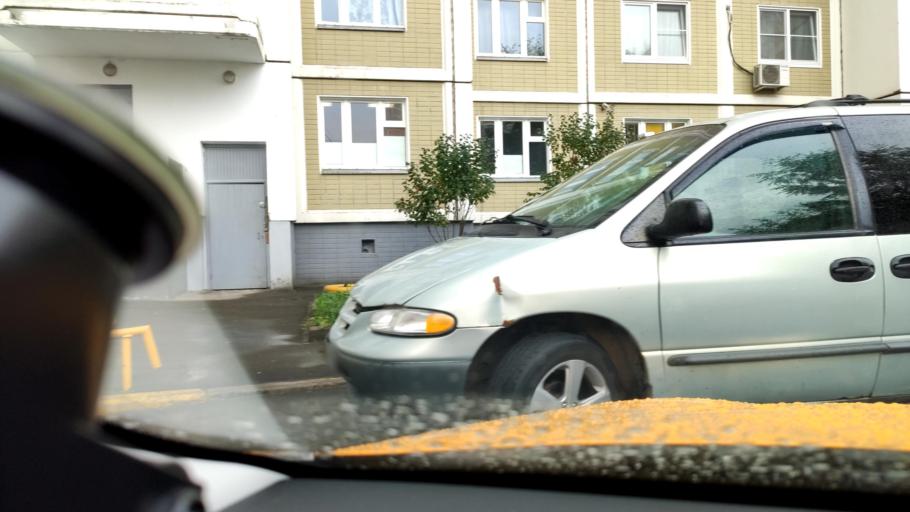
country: RU
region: Moscow
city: Vagonoremont
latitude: 55.9127
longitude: 37.5521
